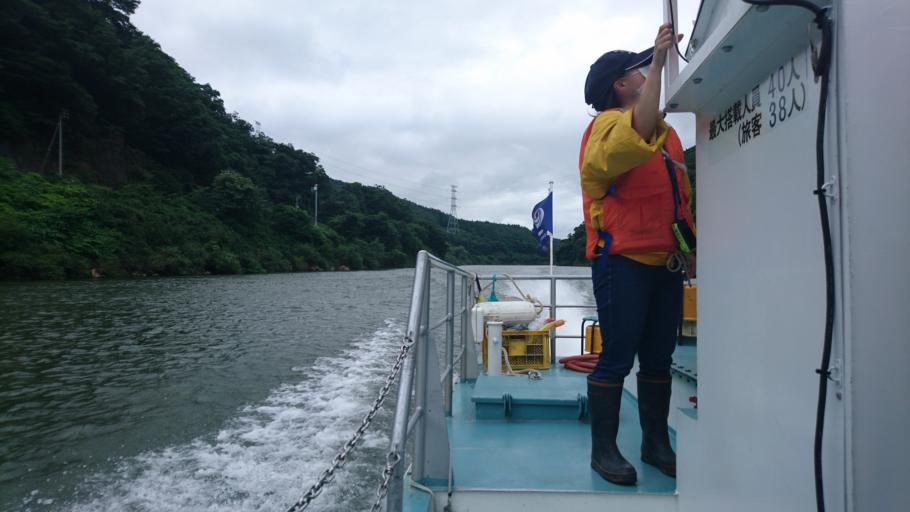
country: JP
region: Iwate
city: Ichinoseki
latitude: 38.9295
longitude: 141.2249
